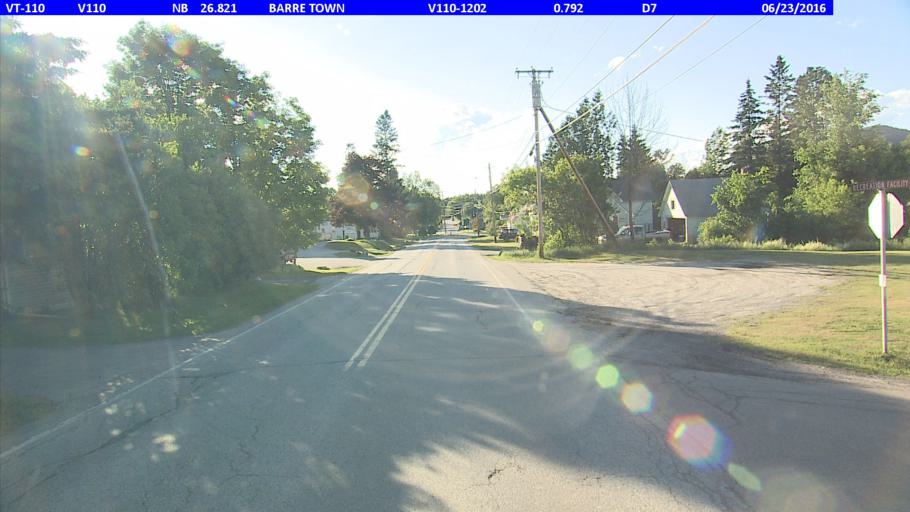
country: US
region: Vermont
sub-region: Washington County
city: South Barre
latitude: 44.1571
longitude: -72.4491
